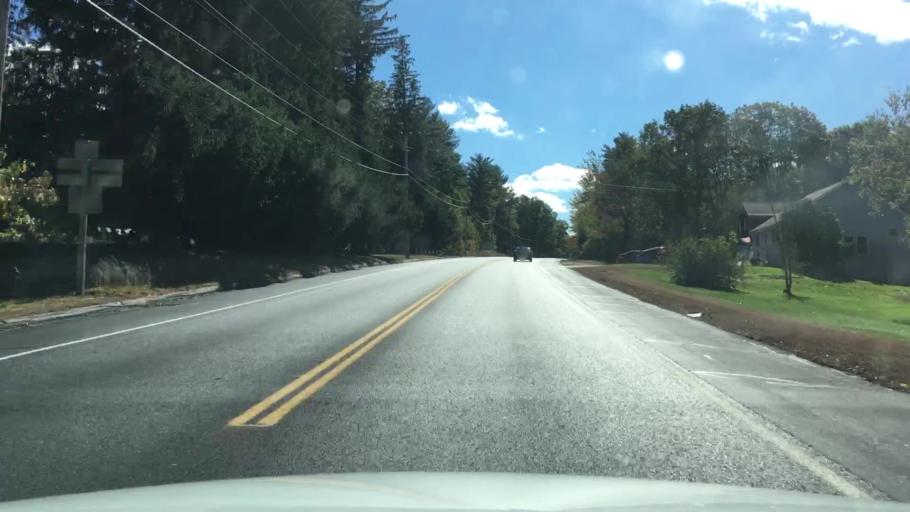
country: US
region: Maine
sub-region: York County
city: Alfred
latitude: 43.4694
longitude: -70.7201
